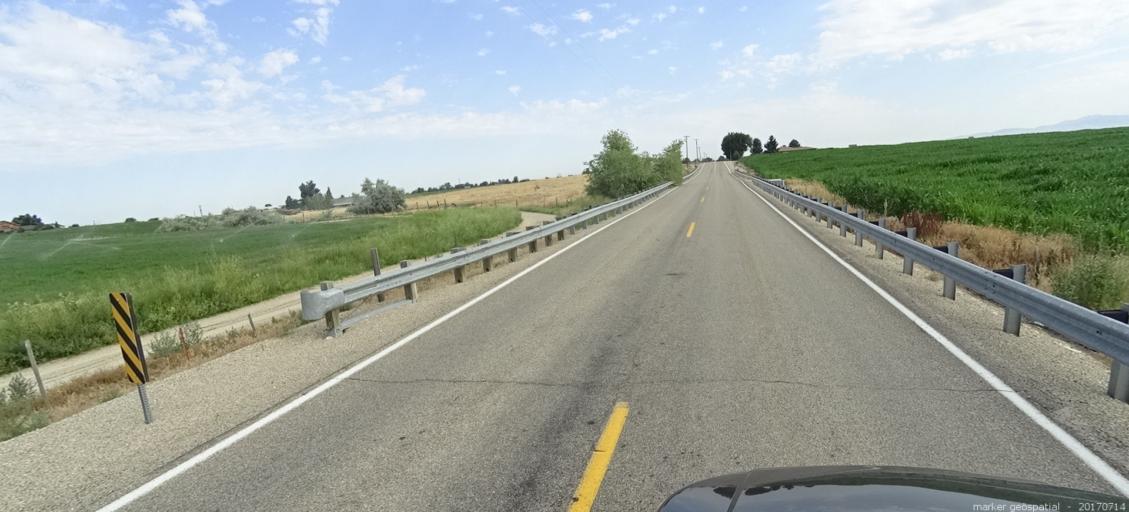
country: US
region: Idaho
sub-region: Ada County
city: Kuna
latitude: 43.4630
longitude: -116.3545
